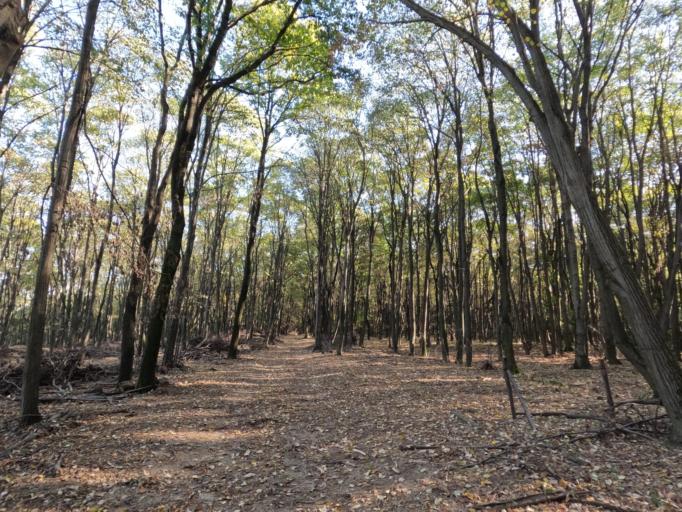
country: HU
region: Tolna
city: Szentgalpuszta
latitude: 46.3188
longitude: 18.6545
